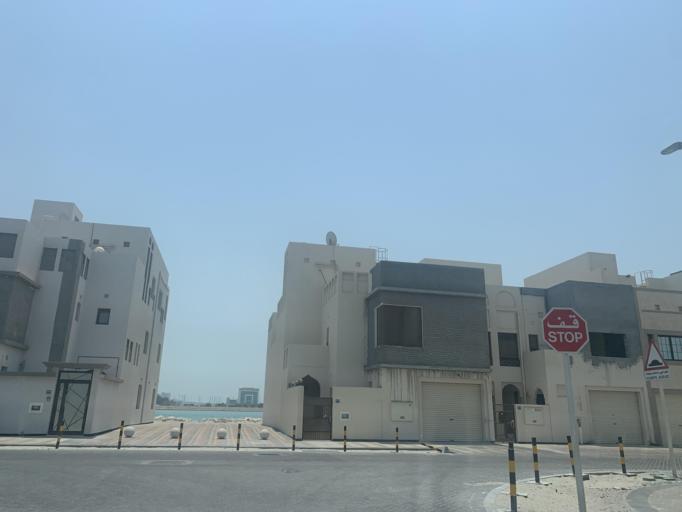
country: BH
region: Muharraq
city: Al Hadd
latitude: 26.2318
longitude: 50.6754
